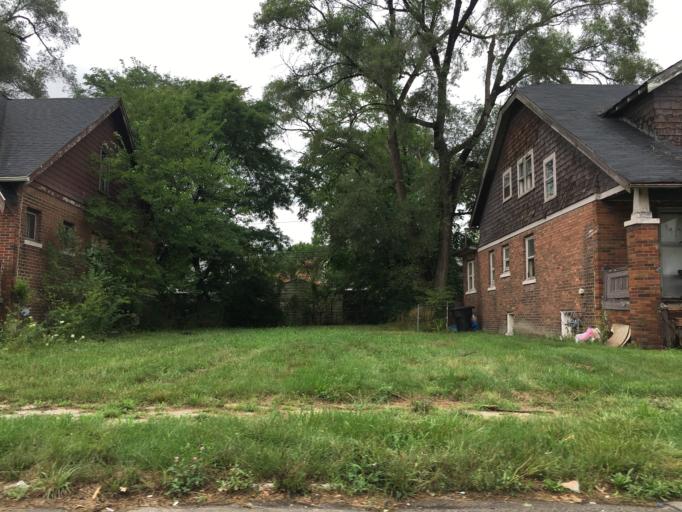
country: US
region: Michigan
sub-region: Wayne County
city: Highland Park
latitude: 42.4077
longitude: -83.1526
